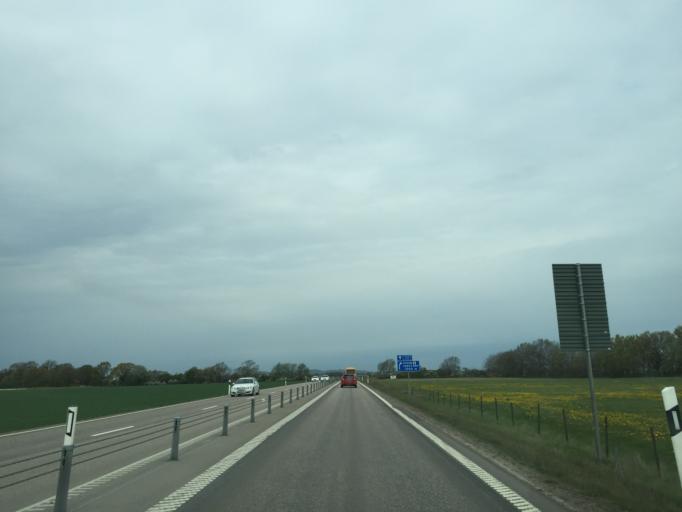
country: SE
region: Skane
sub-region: Hoganas Kommun
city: Hoganas
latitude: 56.1520
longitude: 12.5947
